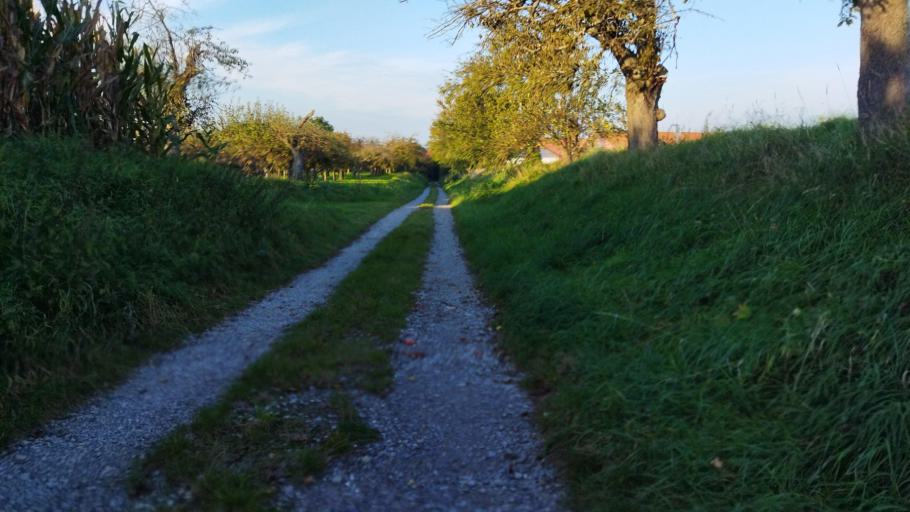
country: DE
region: Baden-Wuerttemberg
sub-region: Regierungsbezirk Stuttgart
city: Ilsfeld
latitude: 49.0395
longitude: 9.2711
